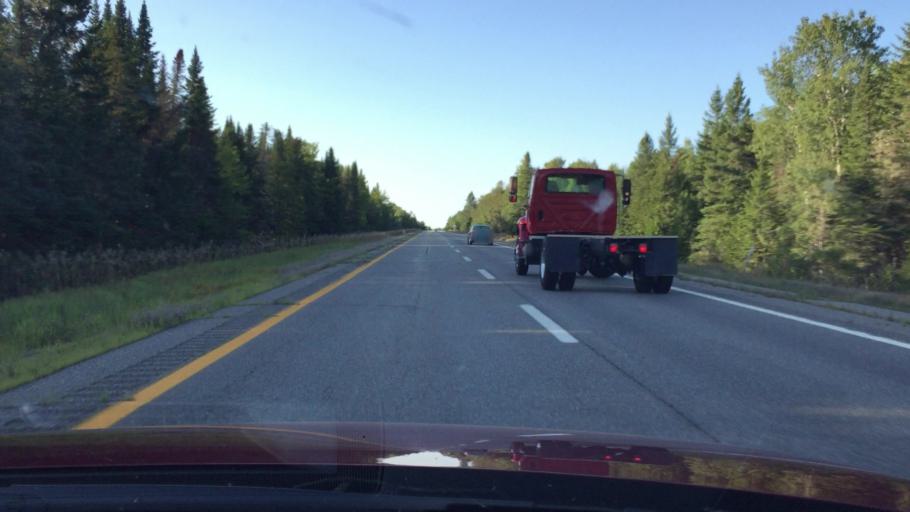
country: US
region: Maine
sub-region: Penobscot County
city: Patten
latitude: 45.8266
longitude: -68.4313
